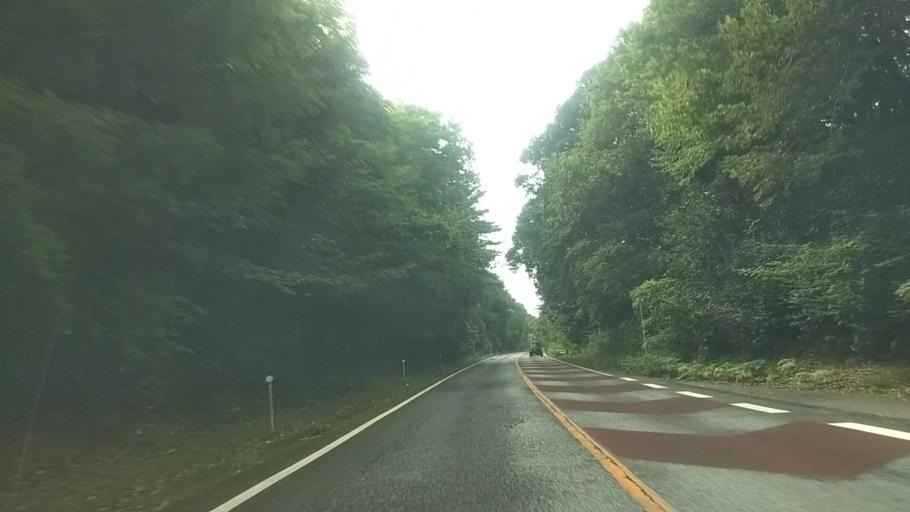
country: JP
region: Chiba
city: Kawaguchi
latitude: 35.2319
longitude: 140.0225
